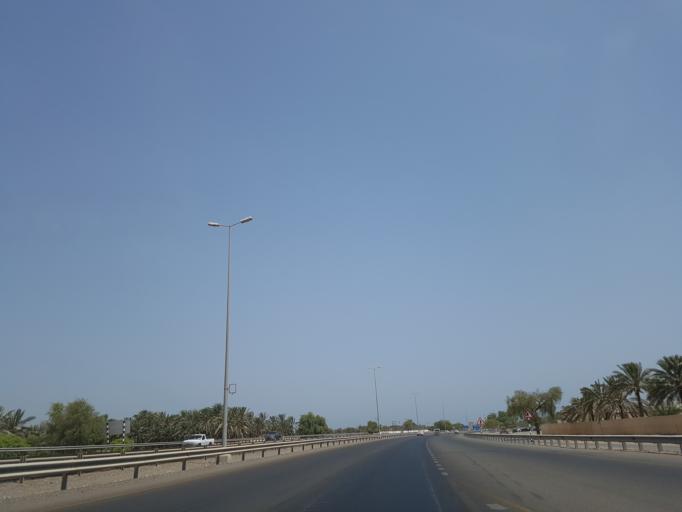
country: OM
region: Al Batinah
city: Saham
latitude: 24.1841
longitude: 56.8567
